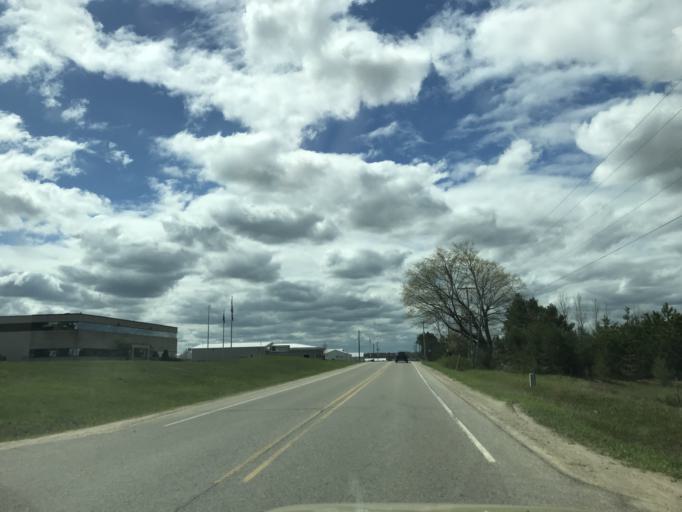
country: US
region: Michigan
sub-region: Otsego County
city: Gaylord
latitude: 45.0376
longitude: -84.7071
